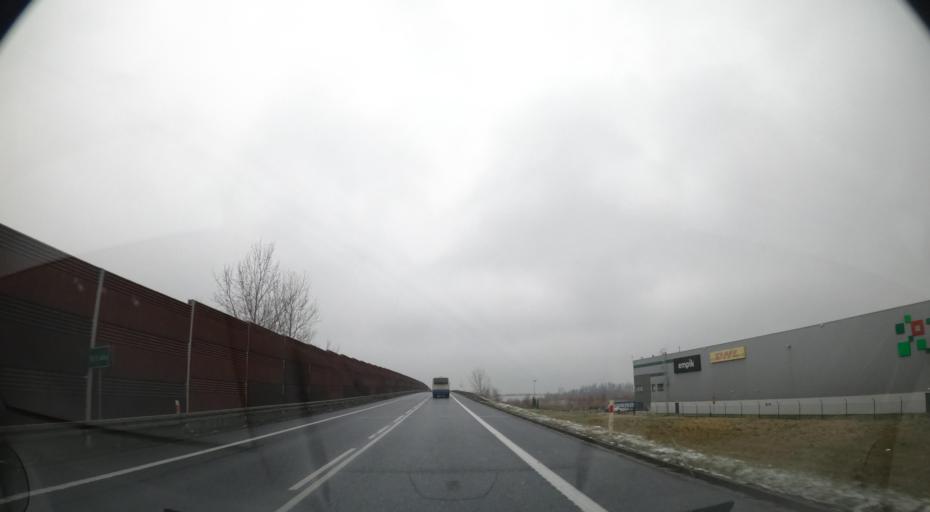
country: PL
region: Masovian Voivodeship
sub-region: Powiat sochaczewski
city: Sochaczew
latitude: 52.2214
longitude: 20.2592
